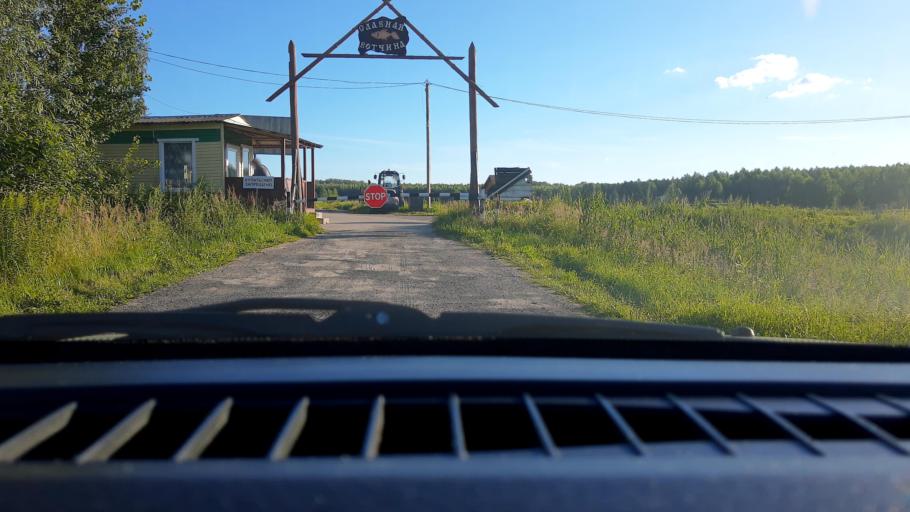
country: RU
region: Nizjnij Novgorod
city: Afonino
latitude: 56.1292
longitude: 44.0581
